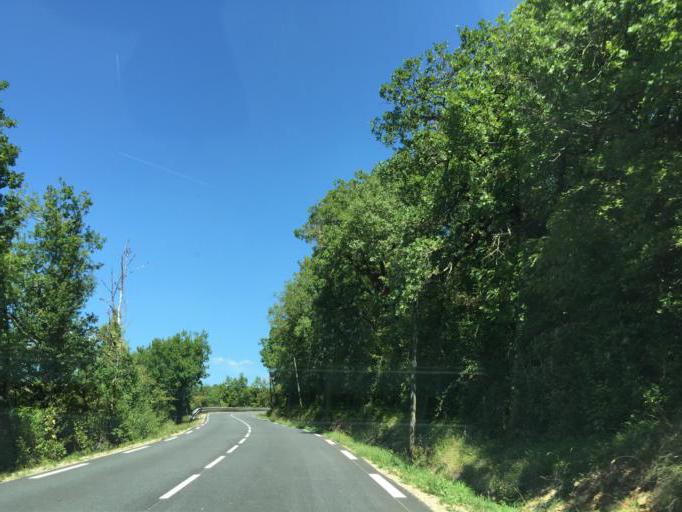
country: FR
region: Midi-Pyrenees
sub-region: Departement de l'Aveyron
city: Espalion
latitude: 44.5382
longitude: 2.7704
